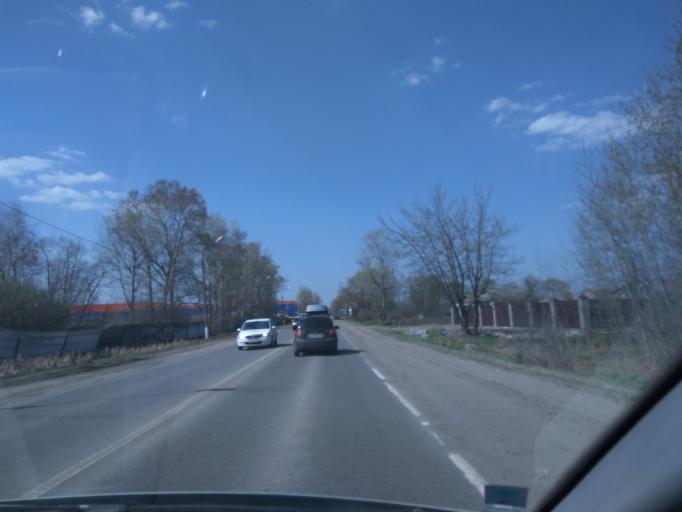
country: RU
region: Moskovskaya
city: Ramenskoye
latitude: 55.5511
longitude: 38.2757
